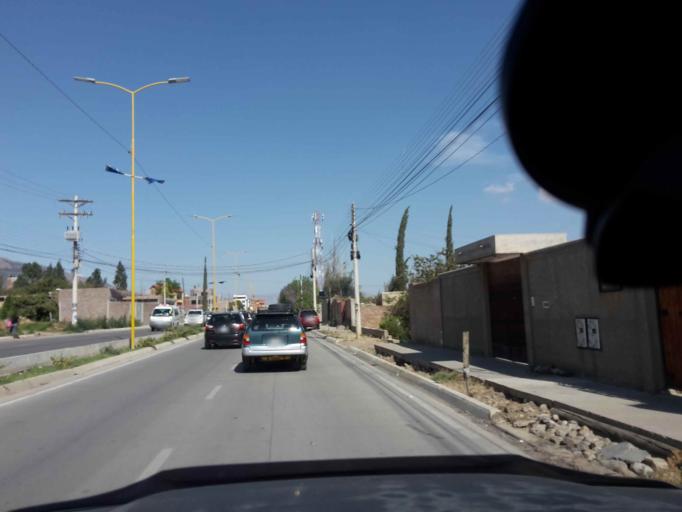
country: BO
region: Cochabamba
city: Cochabamba
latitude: -17.3439
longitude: -66.2012
